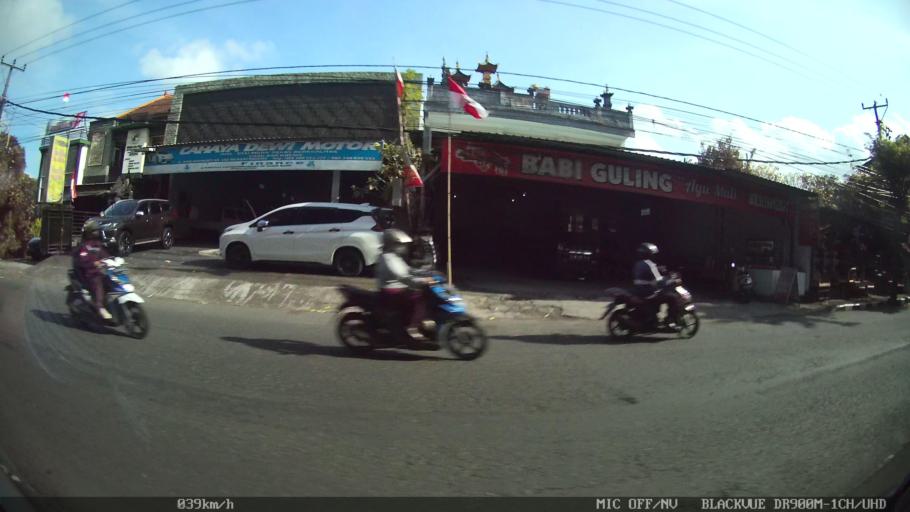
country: ID
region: Bali
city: Banjar Pekenjelodan
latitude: -8.5670
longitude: 115.1752
